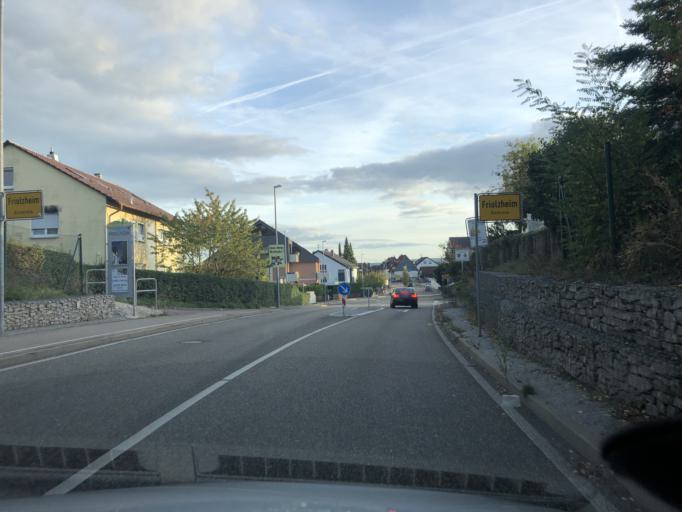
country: DE
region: Baden-Wuerttemberg
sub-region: Karlsruhe Region
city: Friolzheim
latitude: 48.8386
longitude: 8.8318
